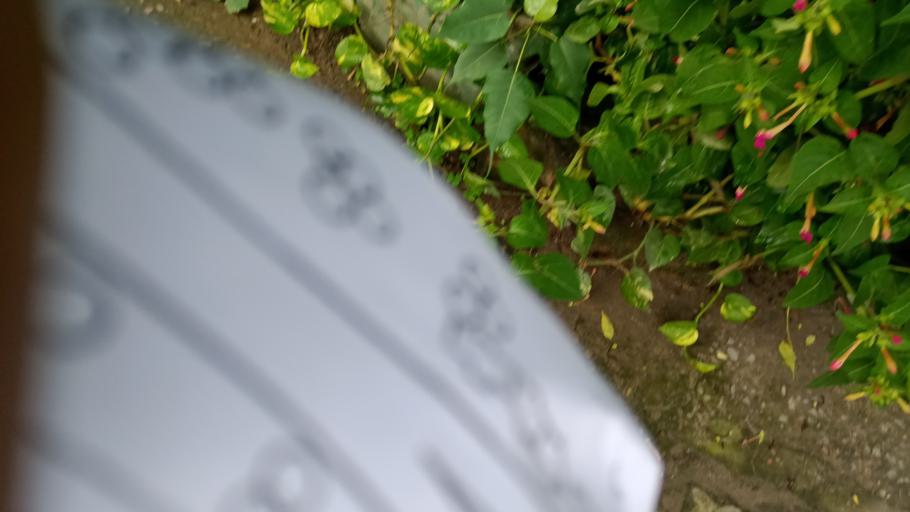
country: IN
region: NCT
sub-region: New Delhi
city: New Delhi
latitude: 28.5777
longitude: 77.2474
